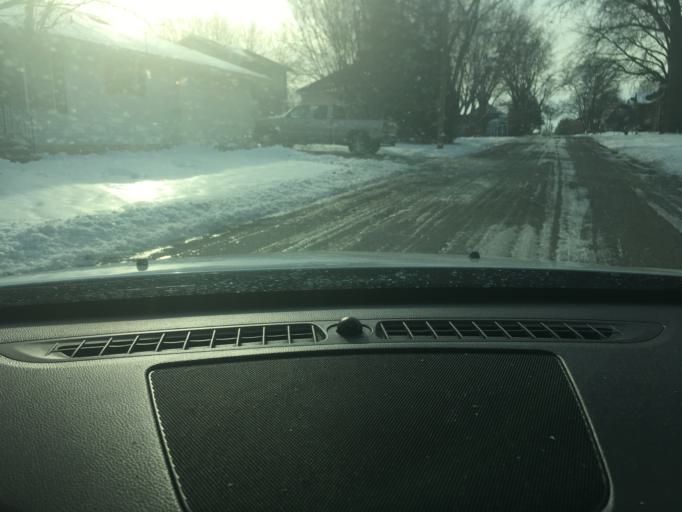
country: US
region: Illinois
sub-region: LaSalle County
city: Peru
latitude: 41.3356
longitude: -89.1144
